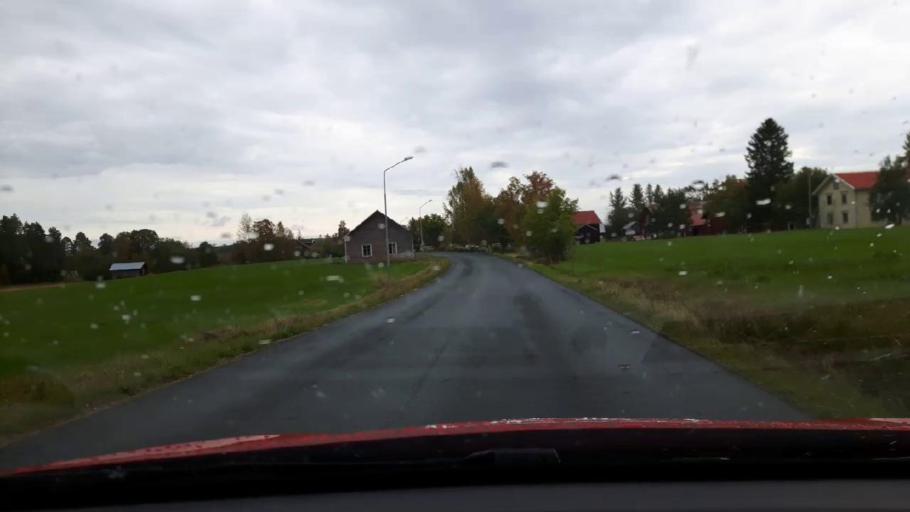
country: SE
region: Jaemtland
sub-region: Bergs Kommun
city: Hoverberg
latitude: 62.9201
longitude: 14.5176
